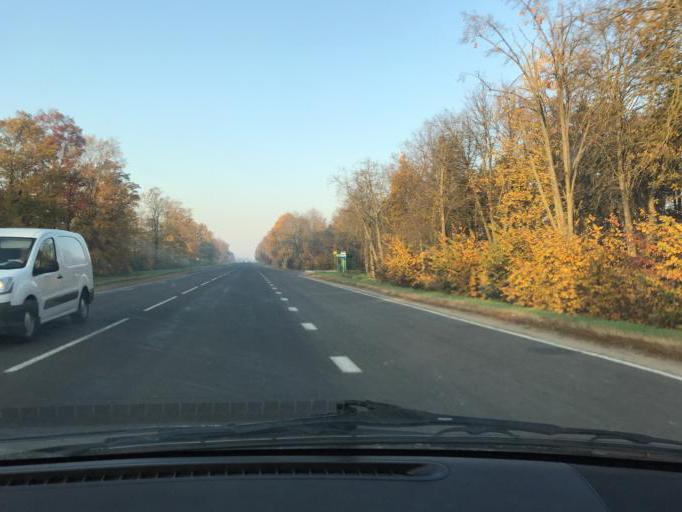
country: BY
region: Minsk
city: Slutsk
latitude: 53.0009
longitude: 27.4253
